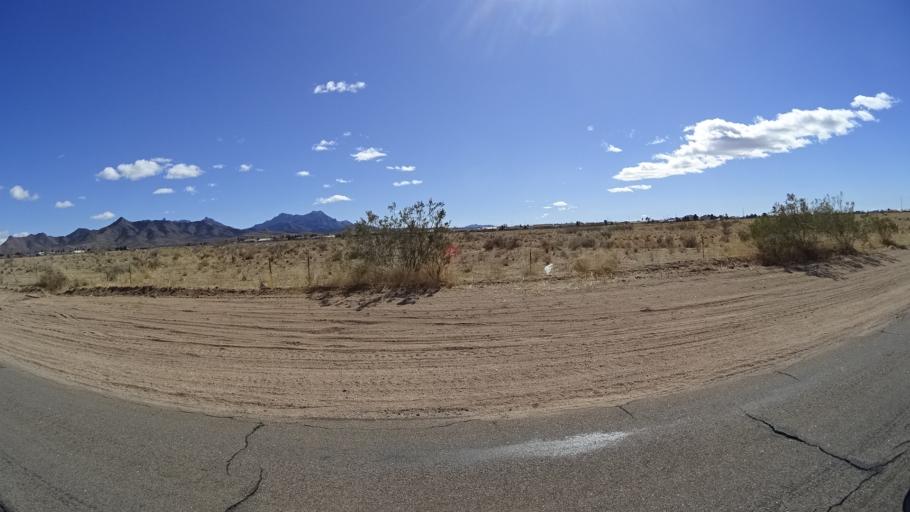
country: US
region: Arizona
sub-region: Mohave County
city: Kingman
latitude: 35.2018
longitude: -113.9831
